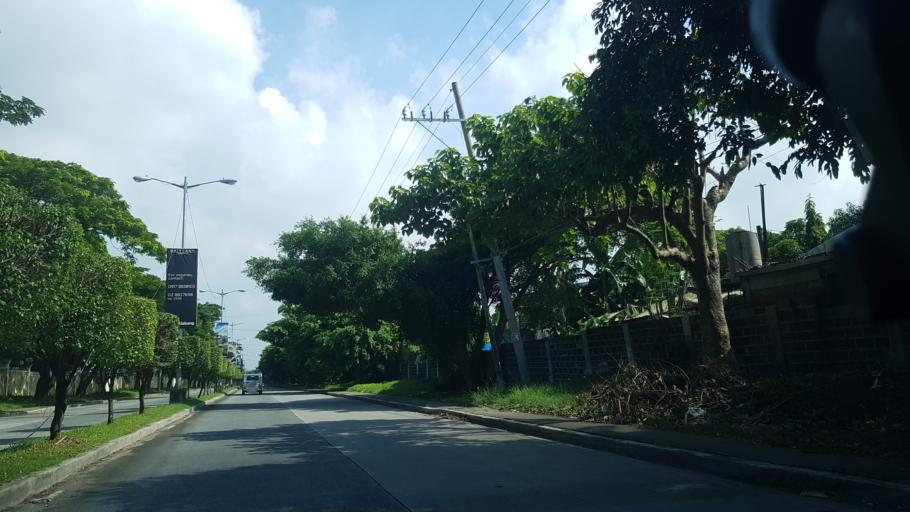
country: PH
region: Calabarzon
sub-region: Province of Laguna
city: Magsaysay
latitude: 14.3653
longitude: 121.0098
